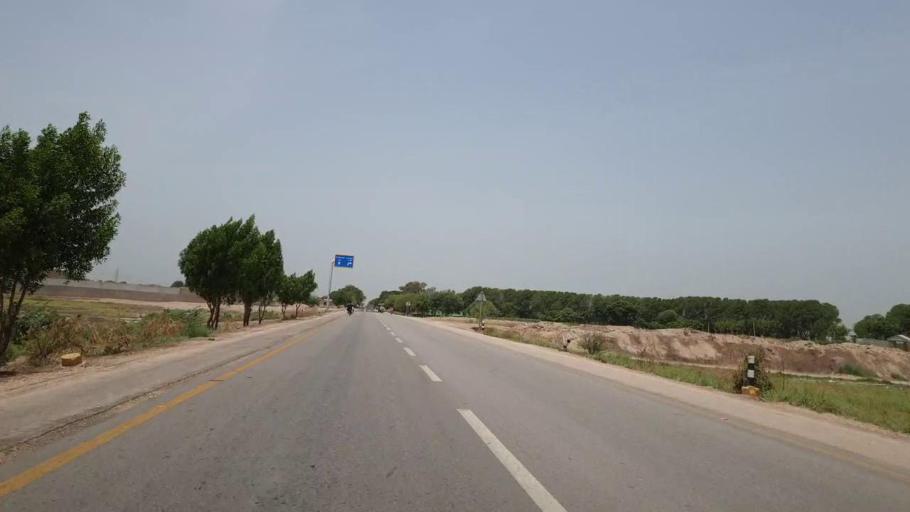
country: PK
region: Sindh
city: Nawabshah
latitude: 26.2463
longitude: 68.4608
